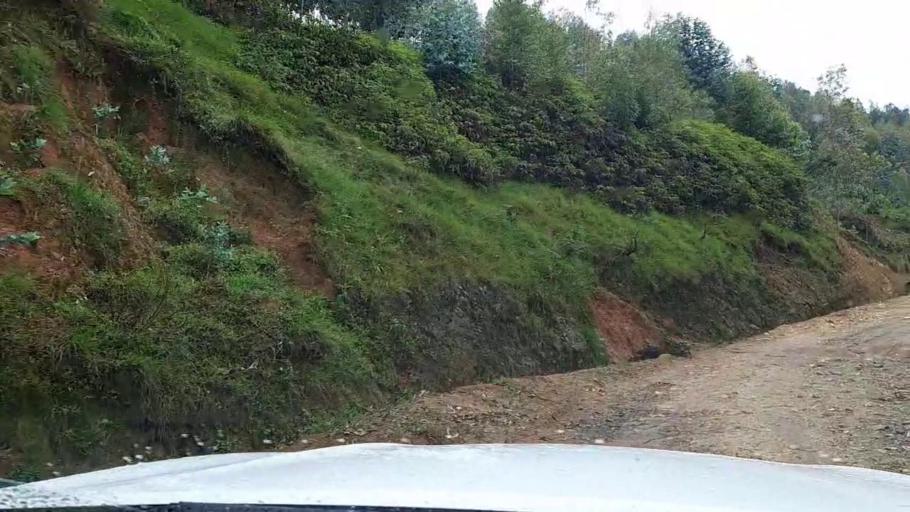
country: RW
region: Southern Province
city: Nzega
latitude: -2.4590
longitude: 29.4918
